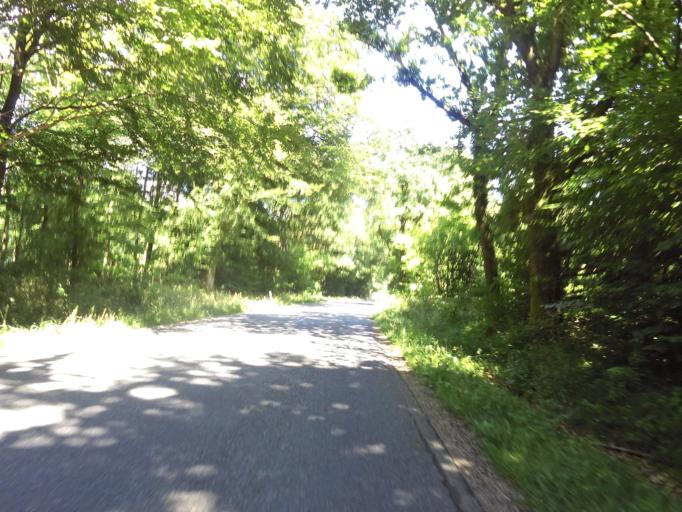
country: DK
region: South Denmark
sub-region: Haderslev Kommune
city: Gram
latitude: 55.3053
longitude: 9.0694
